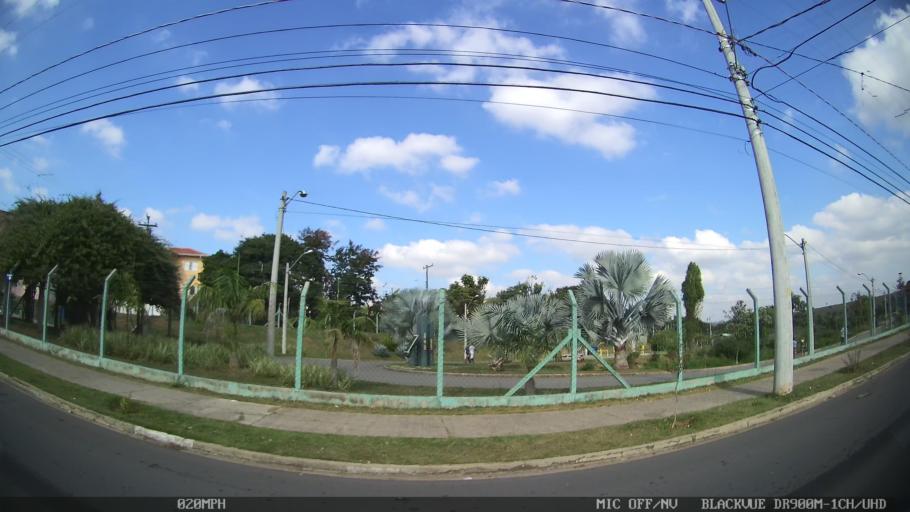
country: BR
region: Sao Paulo
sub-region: Indaiatuba
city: Indaiatuba
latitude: -22.9755
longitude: -47.1742
